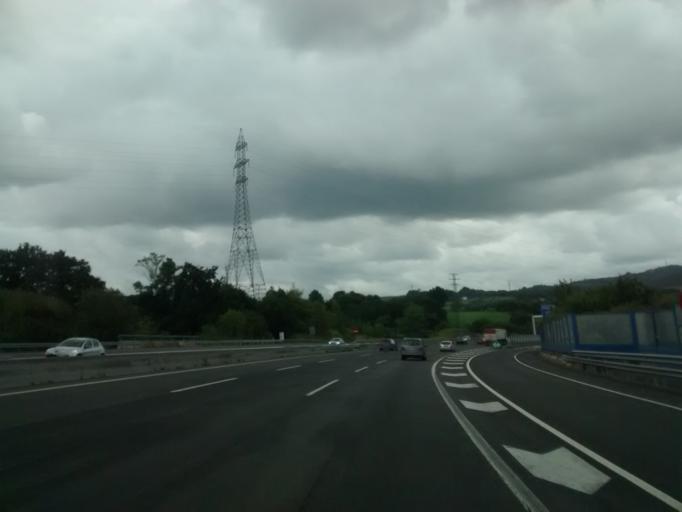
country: ES
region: Basque Country
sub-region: Provincia de Guipuzcoa
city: Lezo
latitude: 43.3084
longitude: -1.8756
